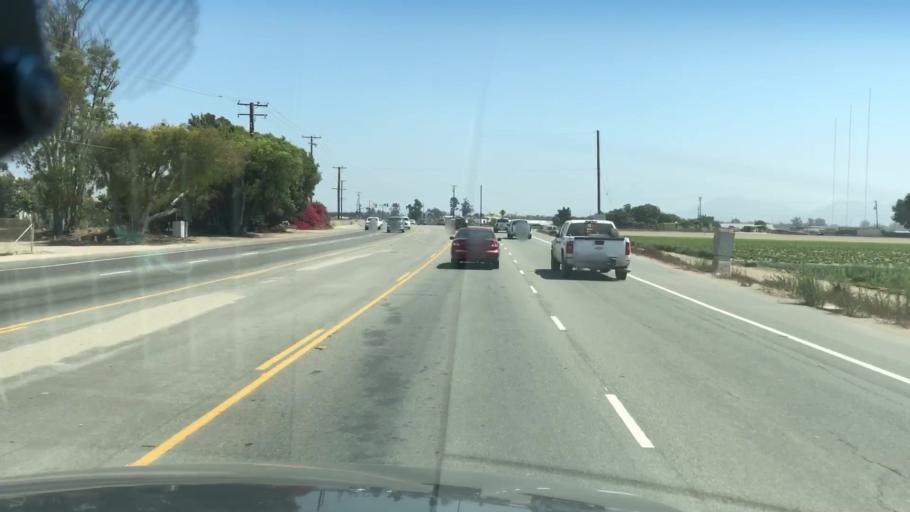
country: US
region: California
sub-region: Ventura County
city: Oxnard
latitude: 34.1676
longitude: -119.1395
